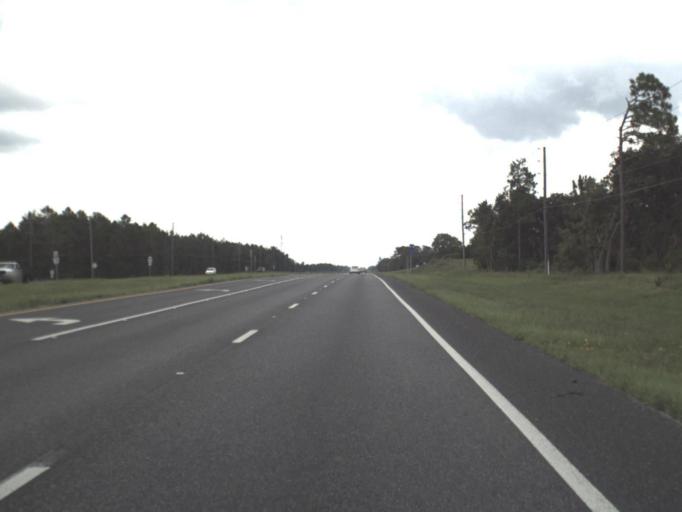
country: US
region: Florida
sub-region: Levy County
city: East Bronson
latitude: 29.4211
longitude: -82.5751
